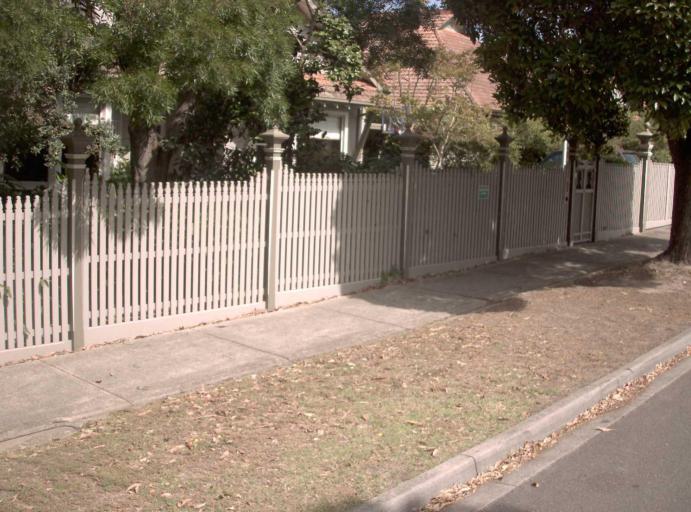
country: AU
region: Victoria
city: Balwyn
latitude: -37.8240
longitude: 145.0654
